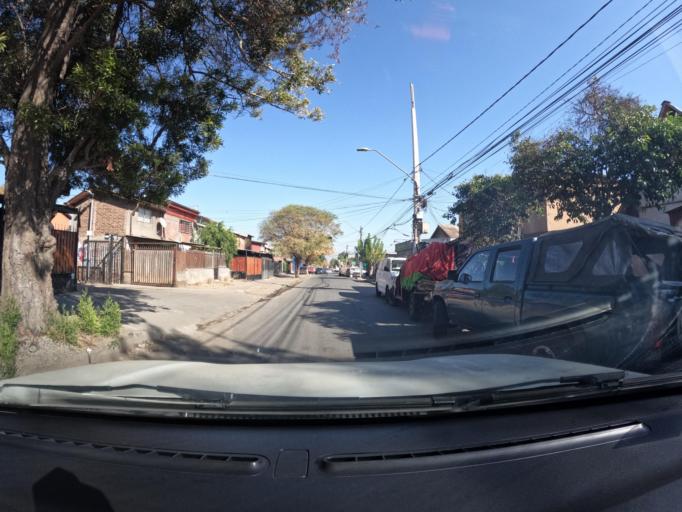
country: CL
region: Santiago Metropolitan
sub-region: Provincia de Santiago
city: Villa Presidente Frei, Nunoa, Santiago, Chile
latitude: -33.4788
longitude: -70.5689
